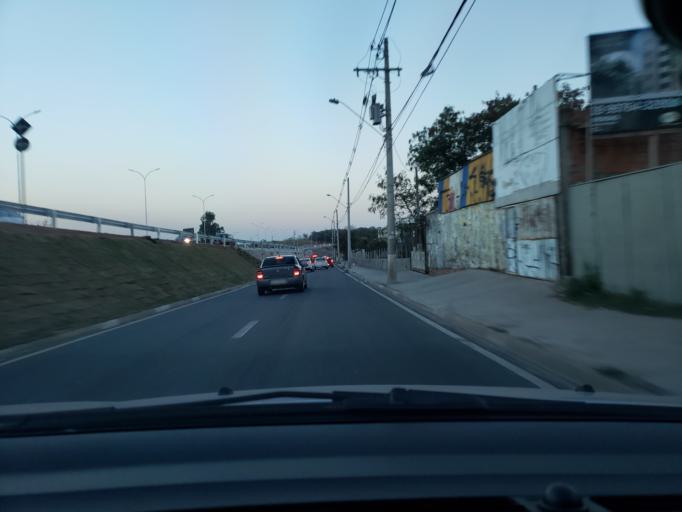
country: BR
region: Sao Paulo
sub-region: Campinas
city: Campinas
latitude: -22.9401
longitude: -47.1421
